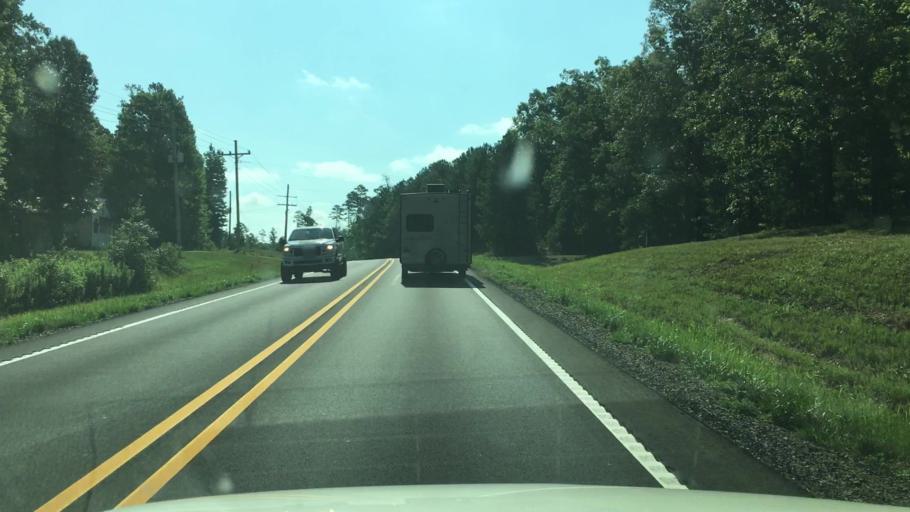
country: US
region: Arkansas
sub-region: Garland County
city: Rockwell
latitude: 34.5227
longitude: -93.3275
